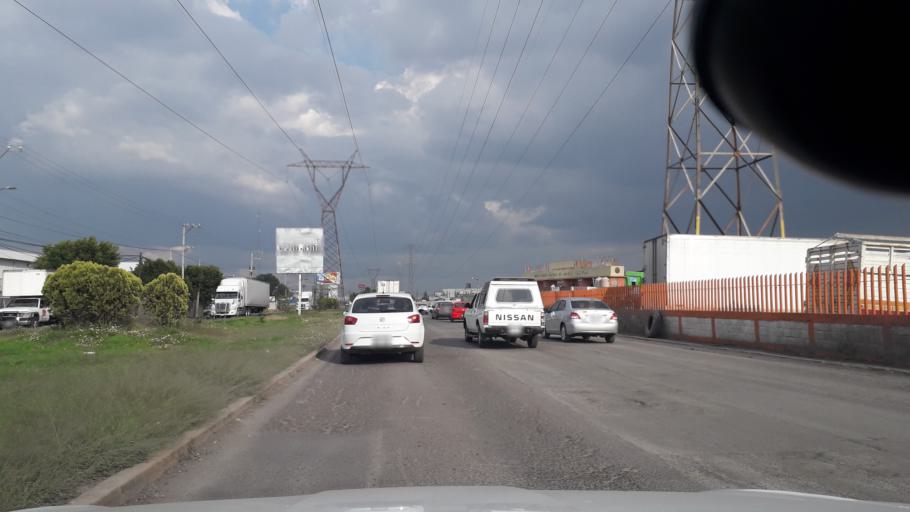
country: MX
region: Mexico
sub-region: Tultitlan
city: Fuentes del Valle
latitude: 19.6399
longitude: -99.1439
